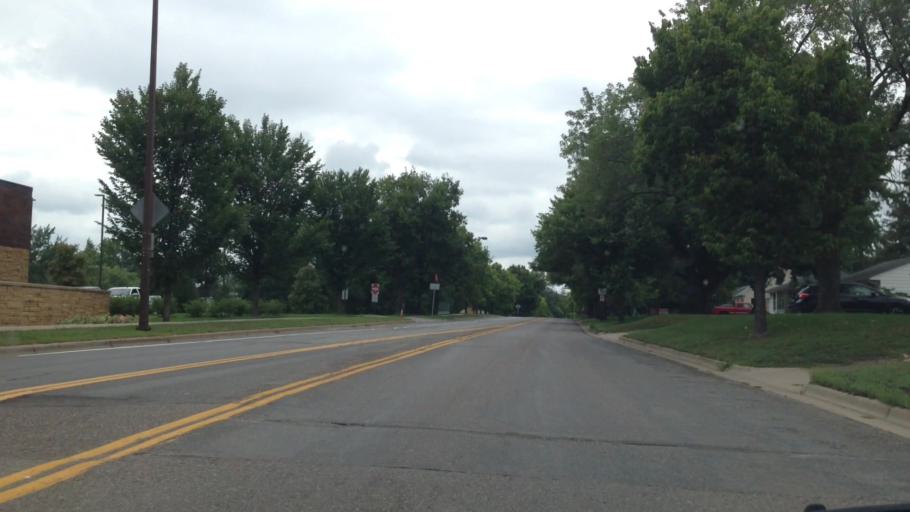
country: US
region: Minnesota
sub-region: Hennepin County
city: Saint Louis Park
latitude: 44.9605
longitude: -93.3709
